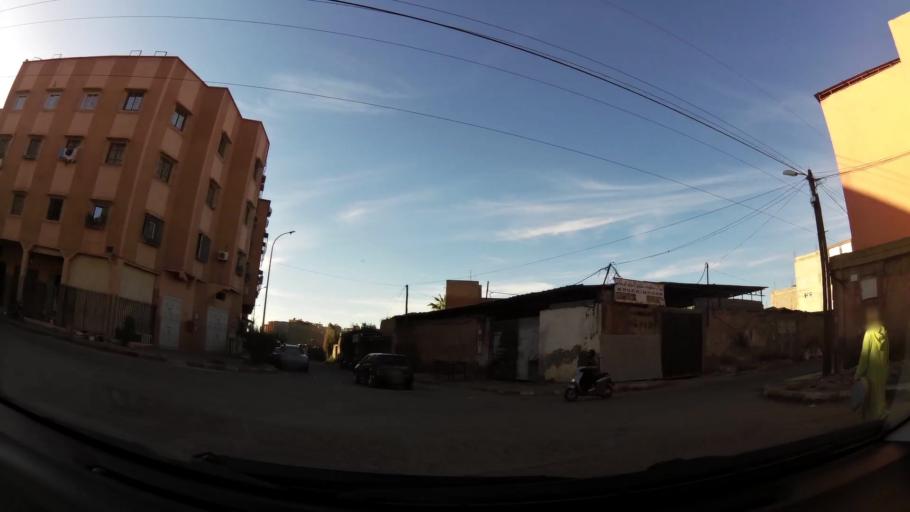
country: MA
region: Marrakech-Tensift-Al Haouz
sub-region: Marrakech
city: Marrakesh
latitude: 31.6166
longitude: -8.0586
